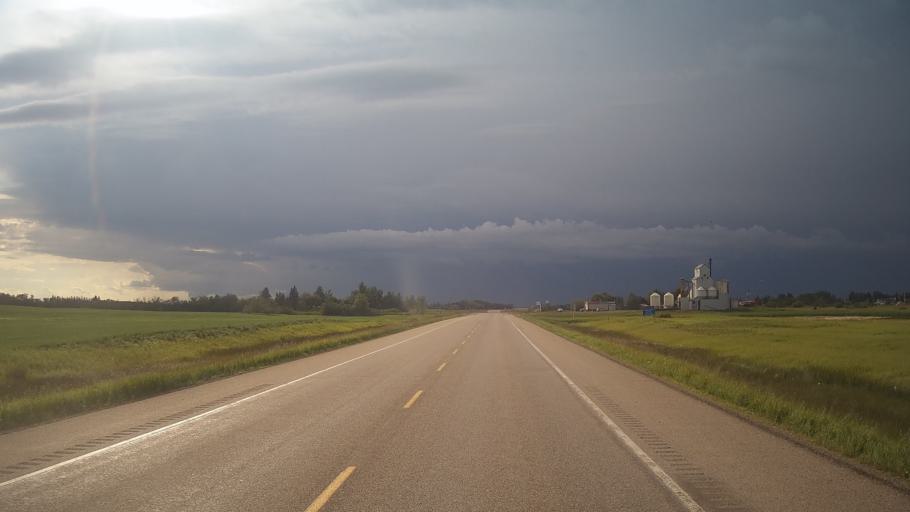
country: CA
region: Alberta
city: Vegreville
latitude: 53.2264
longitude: -112.2326
